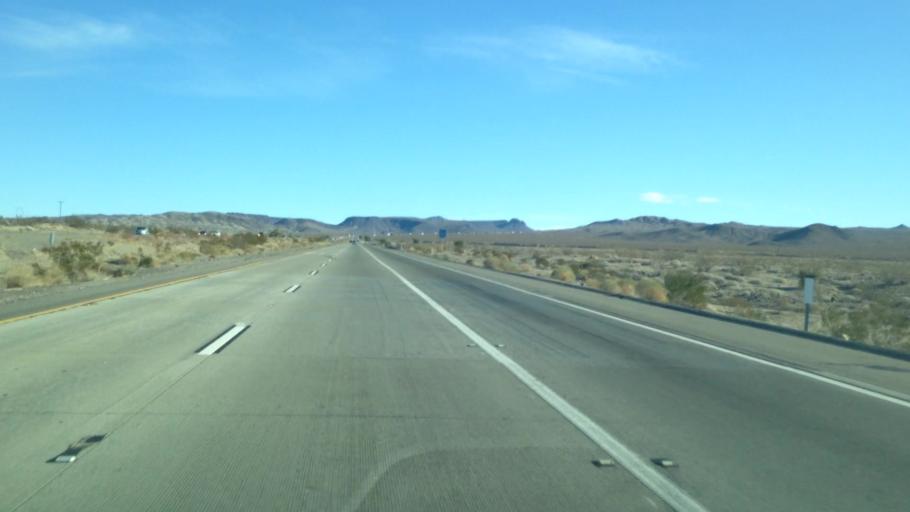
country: US
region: Nevada
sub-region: Clark County
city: Sandy Valley
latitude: 35.3516
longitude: -115.9382
